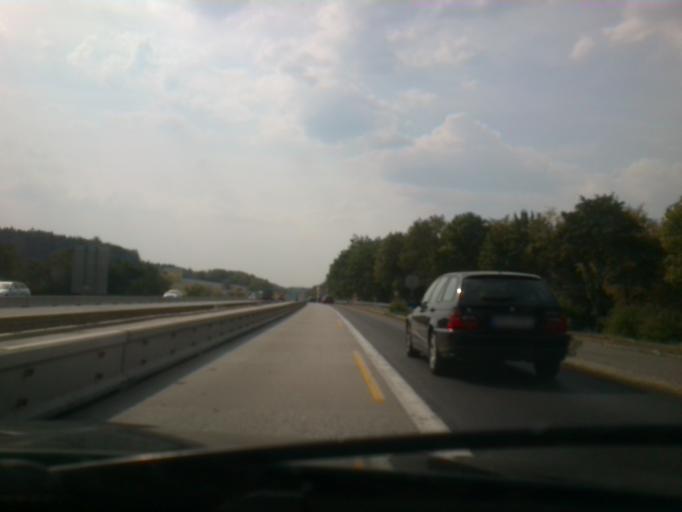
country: CZ
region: Central Bohemia
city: Ondrejov
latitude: 49.8403
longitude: 14.8209
